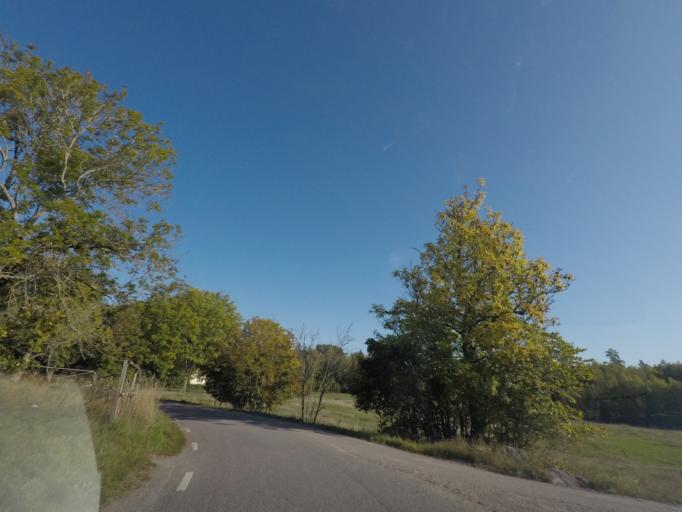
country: SE
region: Vaestmanland
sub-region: Vasteras
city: Vasteras
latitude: 59.5647
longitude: 16.4328
